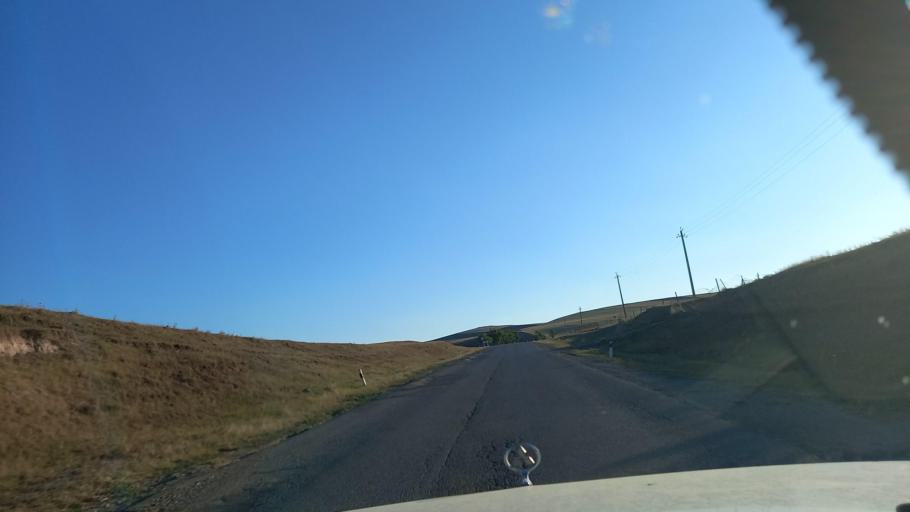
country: AZ
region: Shamkir Rayon
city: Shamkhor
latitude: 40.7695
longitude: 45.9560
